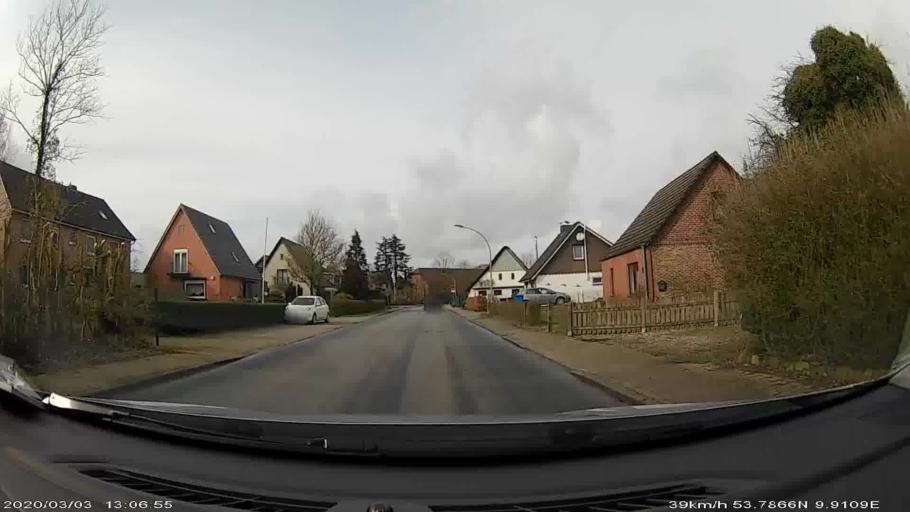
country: DE
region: Schleswig-Holstein
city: Alveslohe
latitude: 53.7872
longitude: 9.9103
